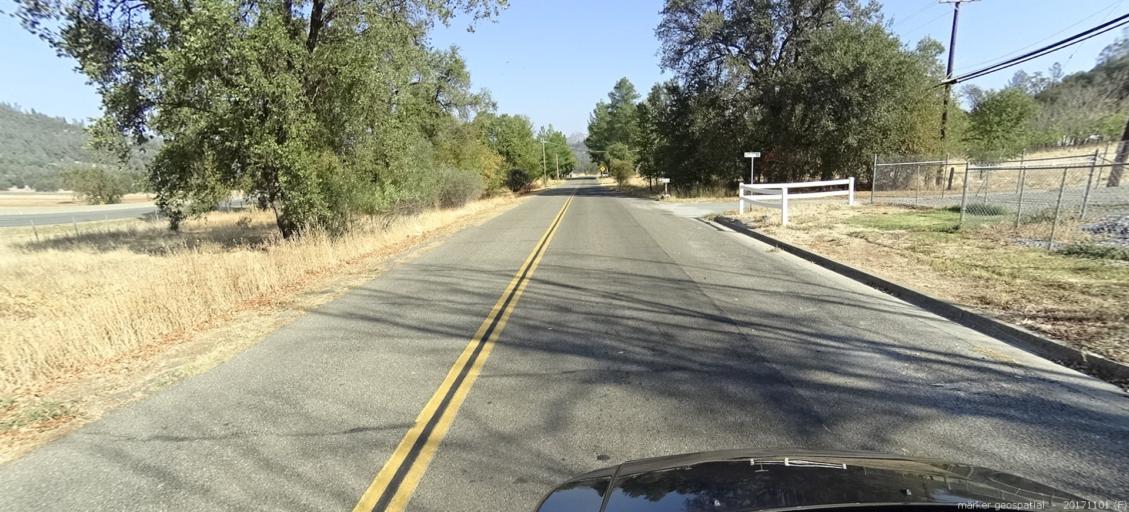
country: US
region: California
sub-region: Shasta County
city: Shasta Lake
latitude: 40.7005
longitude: -122.3396
